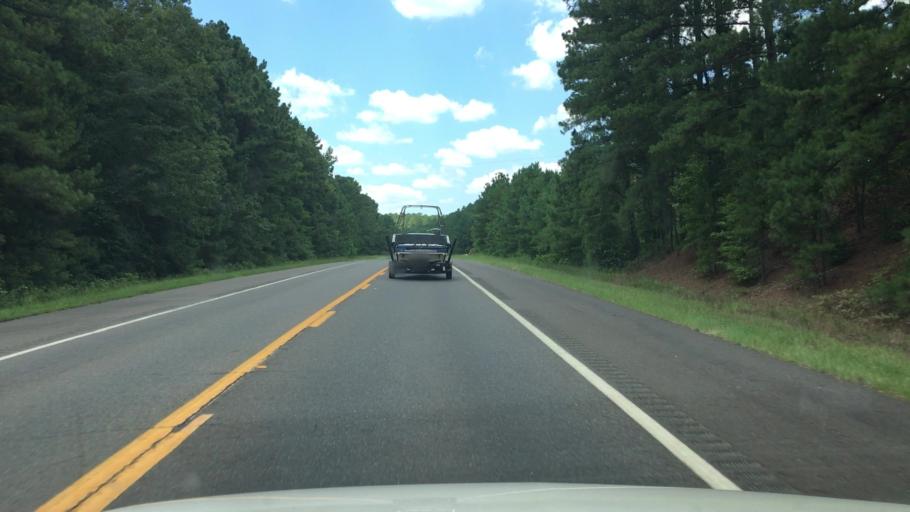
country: US
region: Arkansas
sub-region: Clark County
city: Arkadelphia
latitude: 34.2035
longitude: -93.0784
